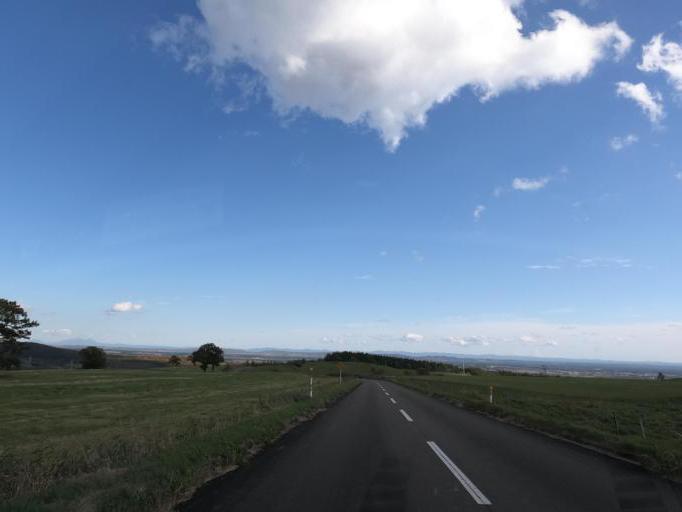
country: JP
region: Hokkaido
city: Otofuke
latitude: 43.2777
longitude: 143.2285
